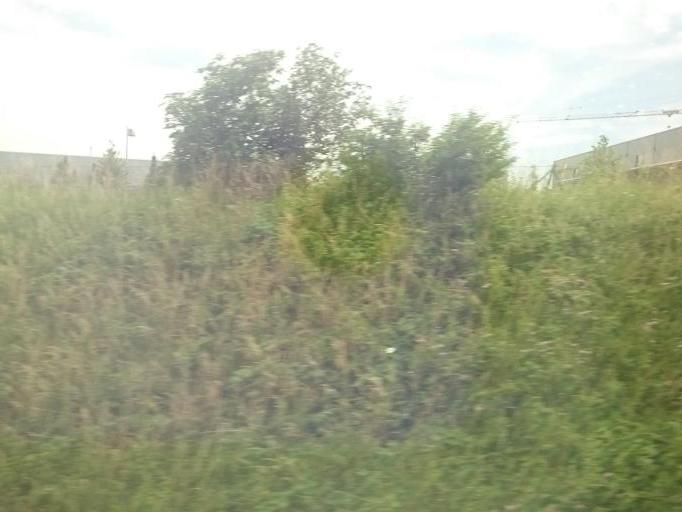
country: DE
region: Bavaria
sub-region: Upper Bavaria
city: Haar
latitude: 48.1213
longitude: 11.6840
